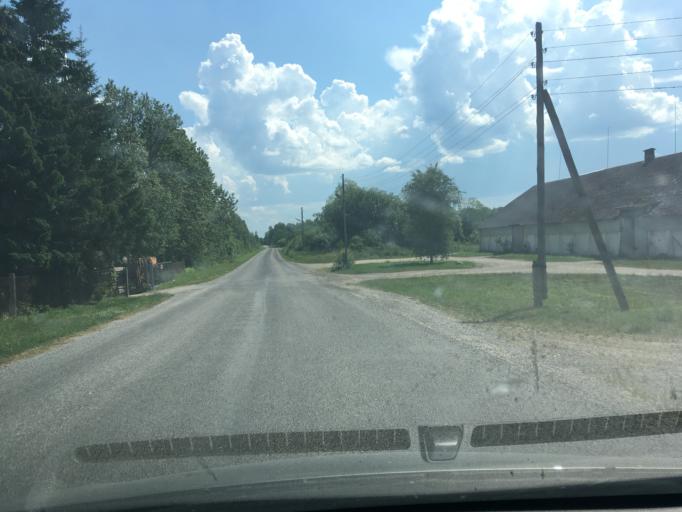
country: EE
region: Laeaene
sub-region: Lihula vald
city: Lihula
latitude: 58.7249
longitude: 23.9538
